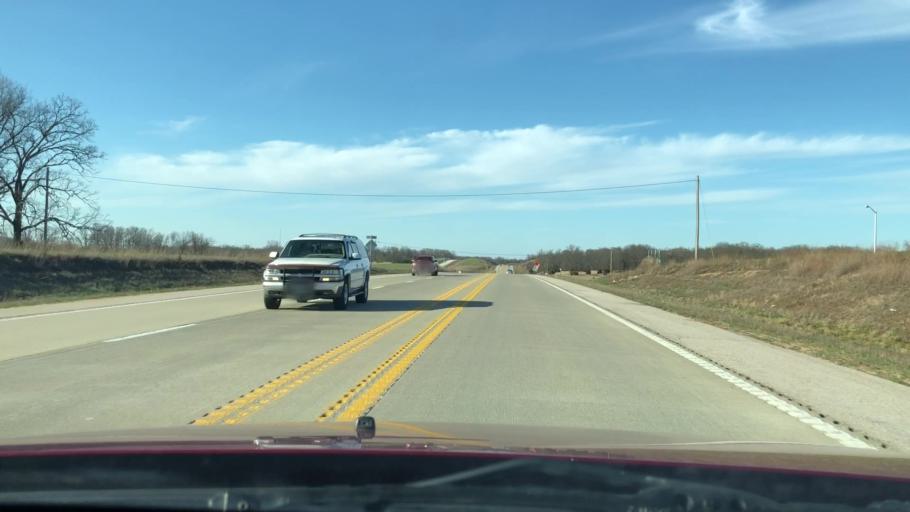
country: US
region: Missouri
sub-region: Camden County
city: Camdenton
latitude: 37.9489
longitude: -92.7155
